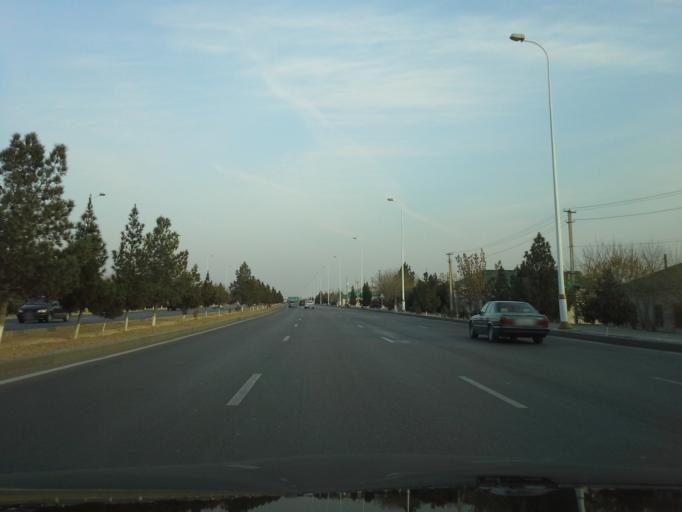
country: TM
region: Ahal
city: Abadan
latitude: 38.0294
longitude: 58.2327
